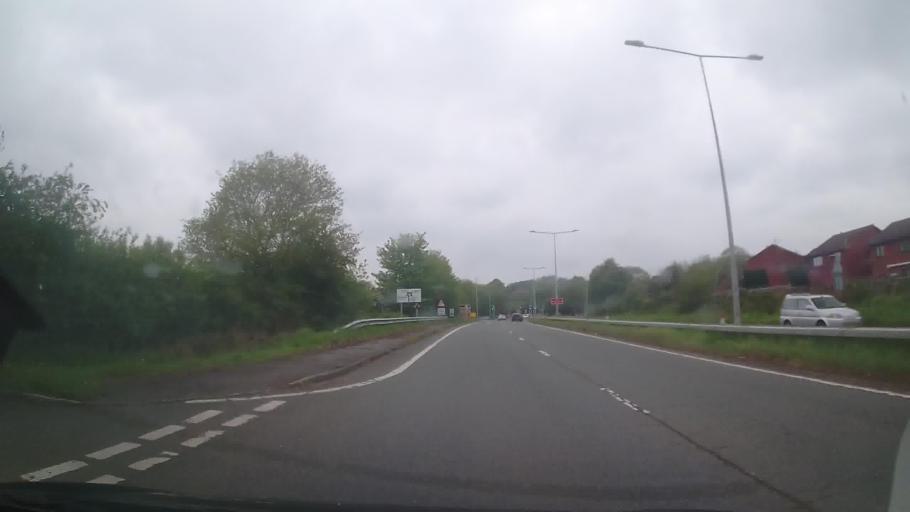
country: GB
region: Wales
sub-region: Wrexham
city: Ruabon
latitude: 52.9841
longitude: -3.0432
